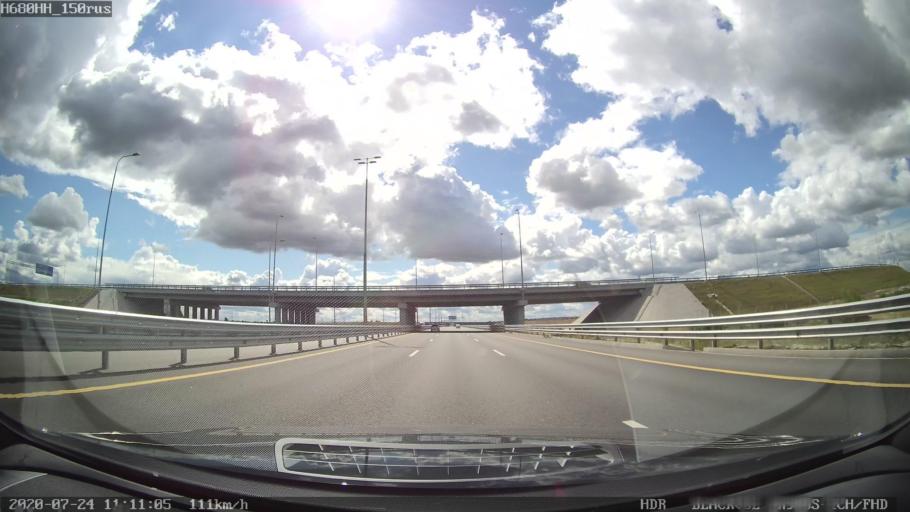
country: RU
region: St.-Petersburg
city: Tyarlevo
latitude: 59.7280
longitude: 30.5113
